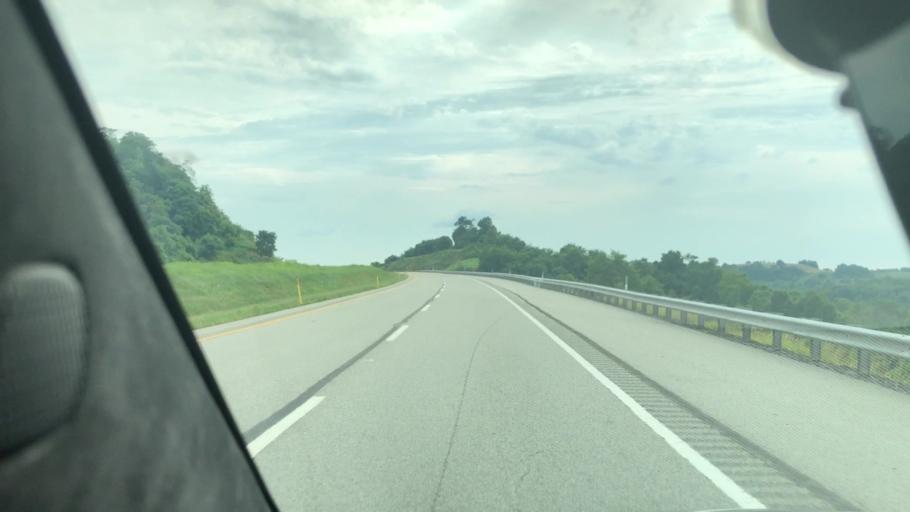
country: US
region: Pennsylvania
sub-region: Washington County
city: Gastonville
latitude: 40.2674
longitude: -79.9721
